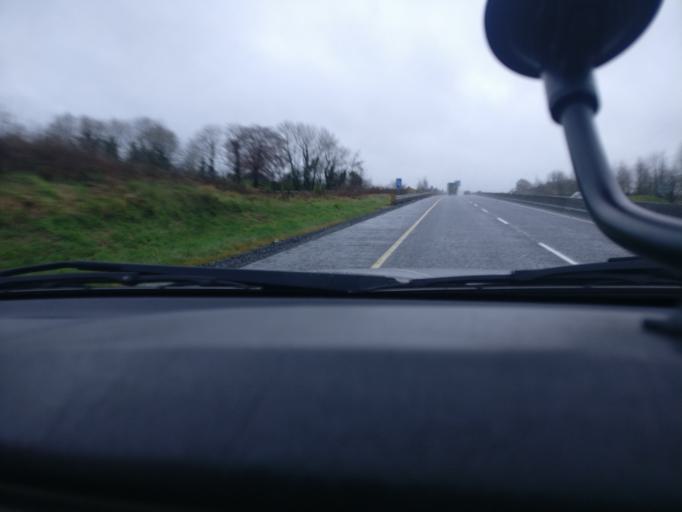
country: IE
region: Leinster
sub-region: An Iarmhi
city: Athlone
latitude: 53.4015
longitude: -7.8440
